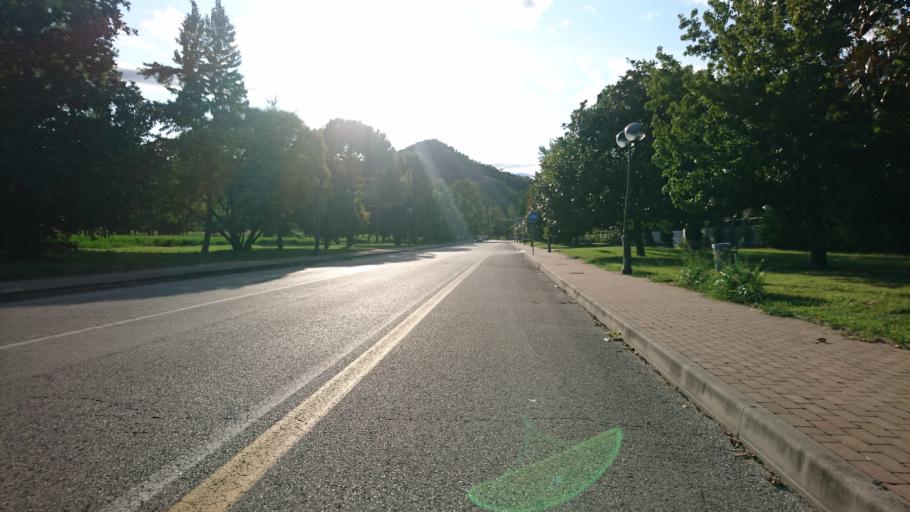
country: IT
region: Veneto
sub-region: Provincia di Padova
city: Montegrotto Terme
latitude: 45.3243
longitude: 11.7831
